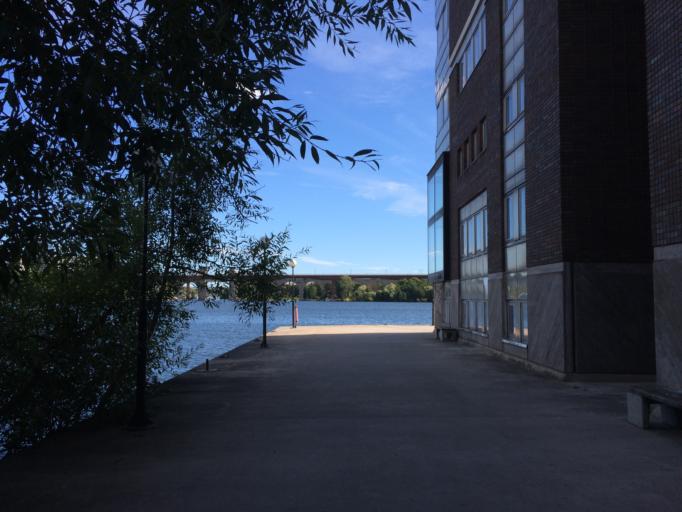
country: SE
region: Stockholm
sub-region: Stockholms Kommun
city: Arsta
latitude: 59.3119
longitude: 18.0325
